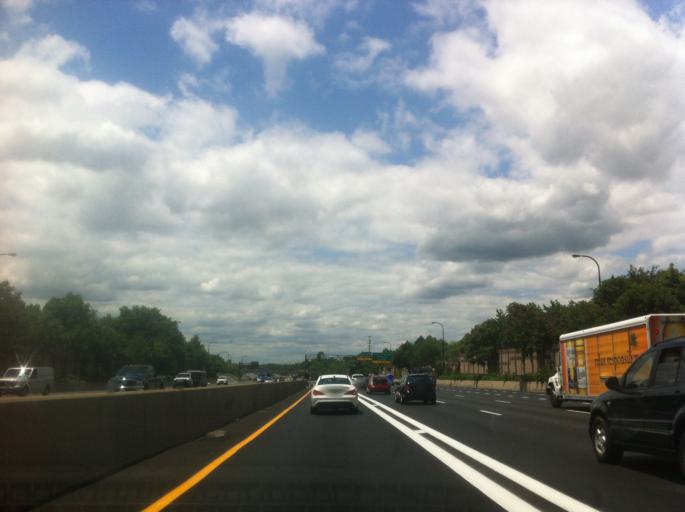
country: US
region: New York
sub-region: Nassau County
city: Syosset
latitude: 40.7989
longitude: -73.4965
